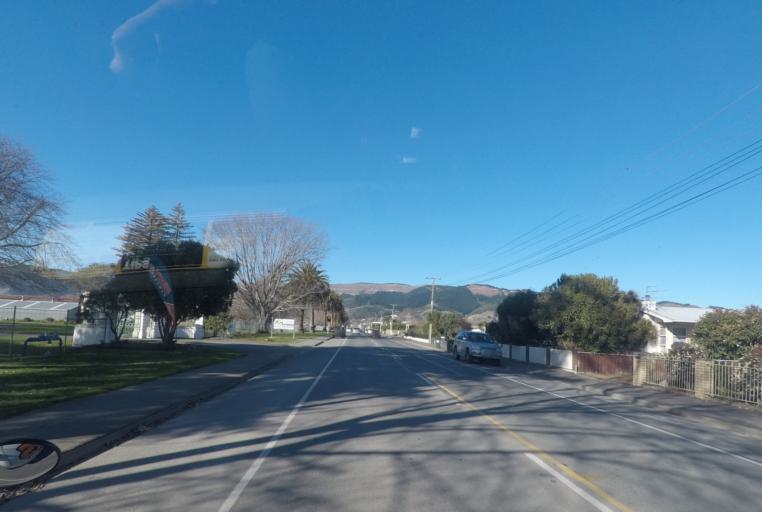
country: NZ
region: Tasman
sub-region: Tasman District
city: Richmond
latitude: -41.3323
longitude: 173.1771
